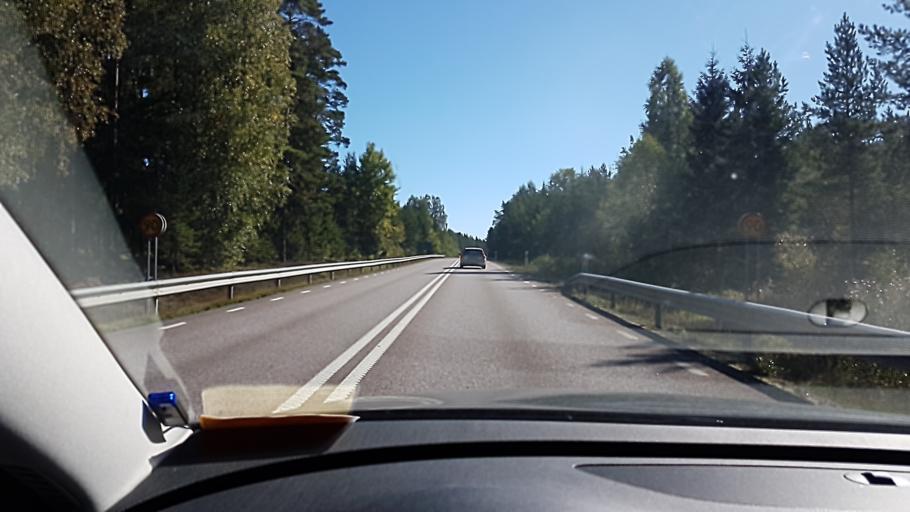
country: SE
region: Kronoberg
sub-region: Lessebo Kommun
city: Lessebo
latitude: 56.7811
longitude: 15.2356
